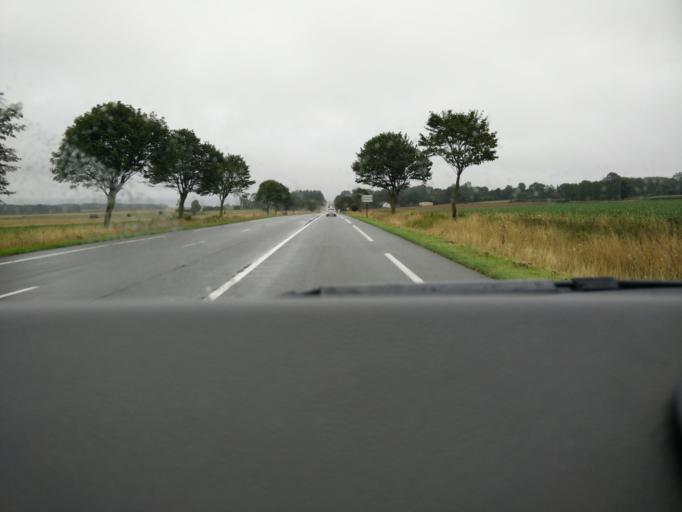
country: FR
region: Nord-Pas-de-Calais
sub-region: Departement du Pas-de-Calais
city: Auchy-les-Hesdin
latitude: 50.3892
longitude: 2.1903
